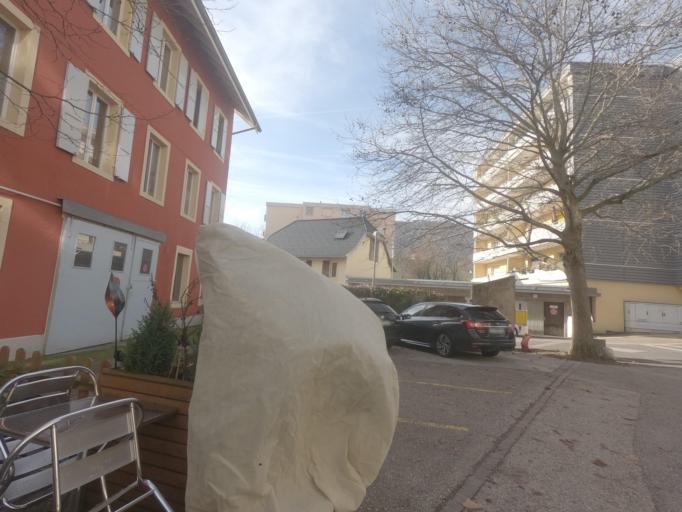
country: CH
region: Neuchatel
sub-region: Boudry District
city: Boudry
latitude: 46.9549
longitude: 6.8318
